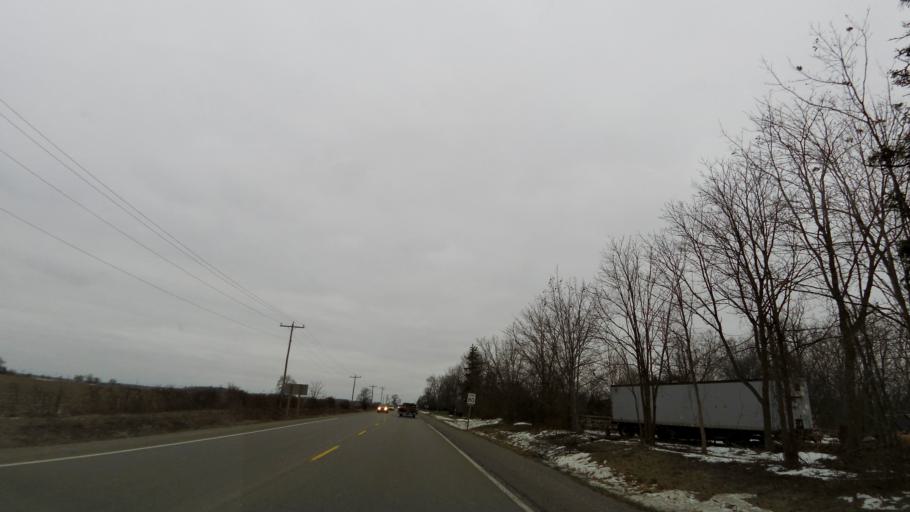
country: CA
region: Ontario
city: Brantford
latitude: 43.1318
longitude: -80.1951
